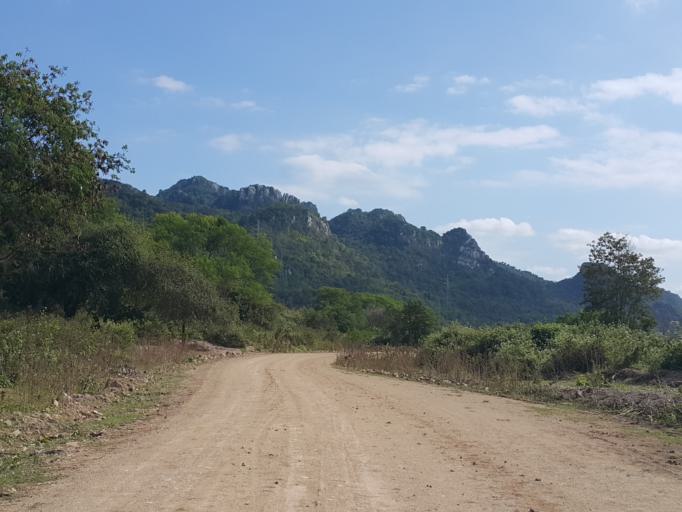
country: TH
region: Lampang
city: Mae Mo
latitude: 18.3313
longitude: 99.7563
